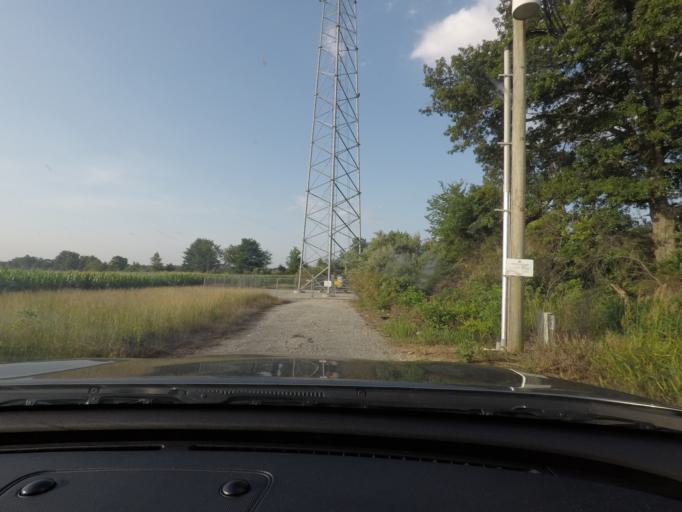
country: US
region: Illinois
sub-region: Jefferson County
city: Mount Vernon
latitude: 38.3653
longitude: -89.0341
